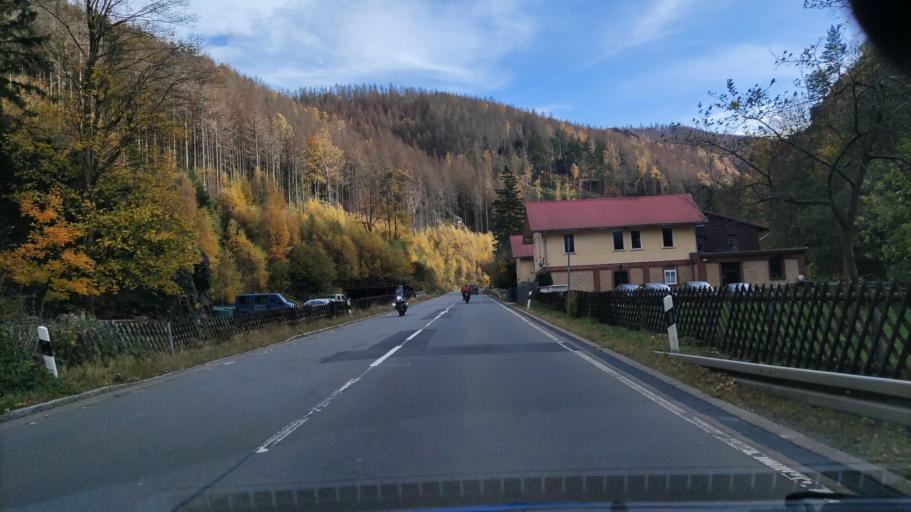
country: DE
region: Lower Saxony
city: Goslar
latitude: 51.8789
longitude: 10.4732
